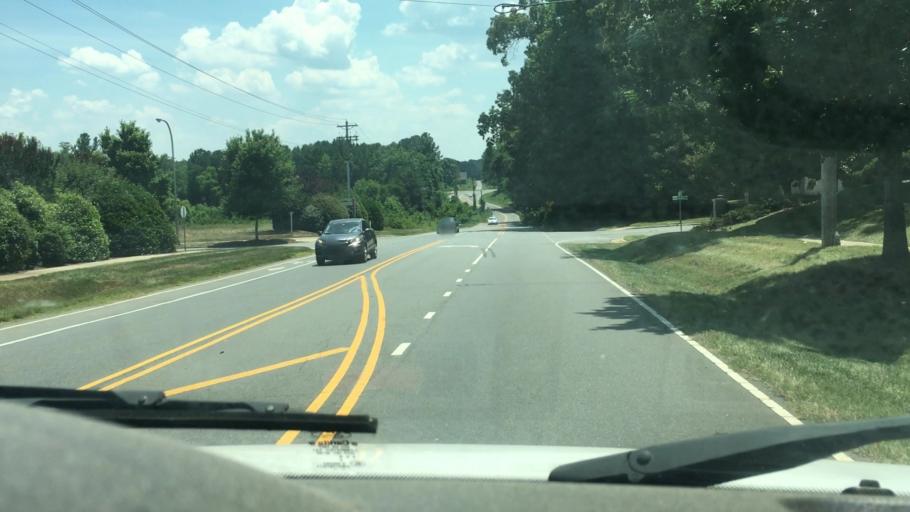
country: US
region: North Carolina
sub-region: Mecklenburg County
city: Huntersville
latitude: 35.4032
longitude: -80.8695
